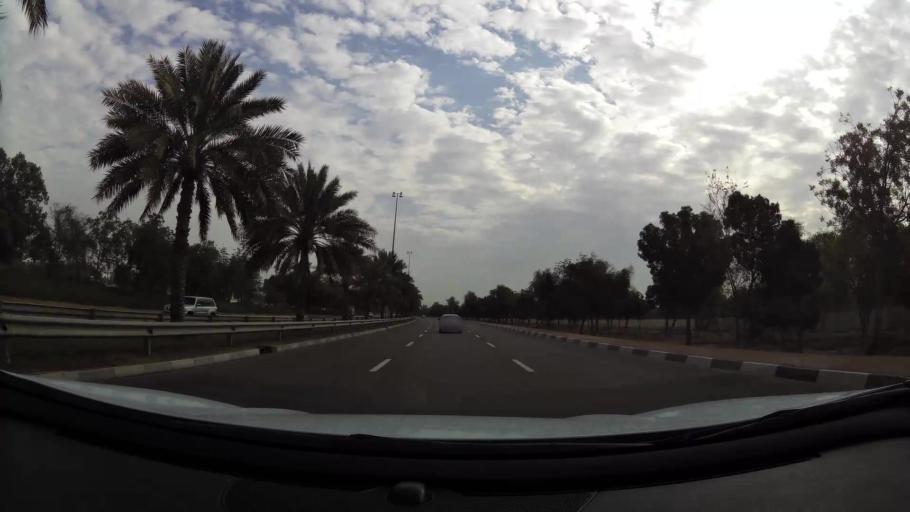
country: AE
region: Abu Dhabi
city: Al Ain
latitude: 24.1788
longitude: 55.6198
